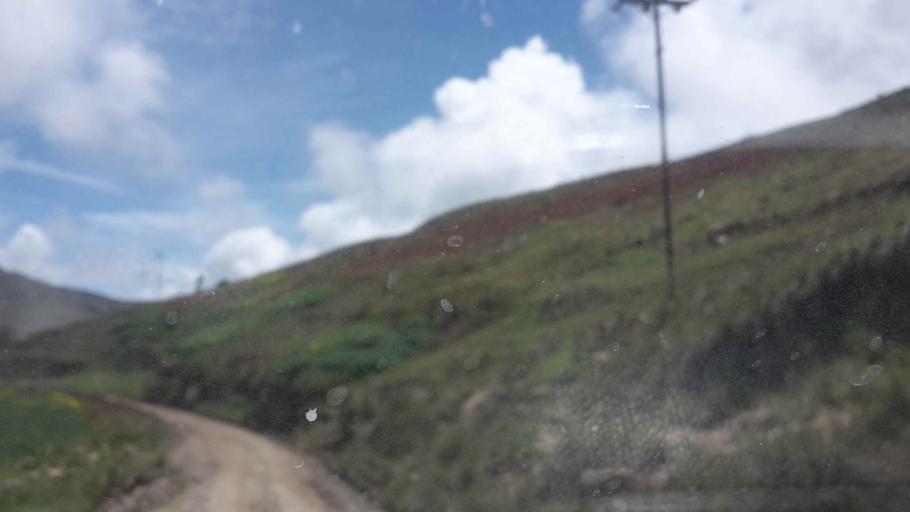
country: BO
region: Cochabamba
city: Cochabamba
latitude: -17.1992
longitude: -66.0840
